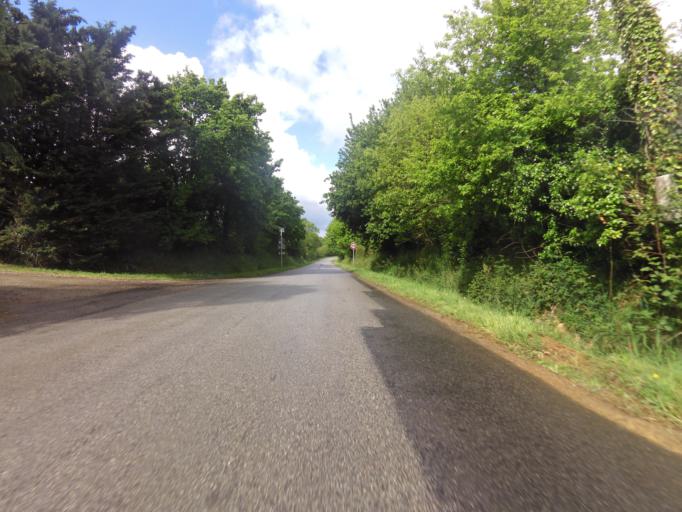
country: FR
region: Brittany
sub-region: Departement du Morbihan
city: Plougoumelen
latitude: 47.6521
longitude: -2.8949
